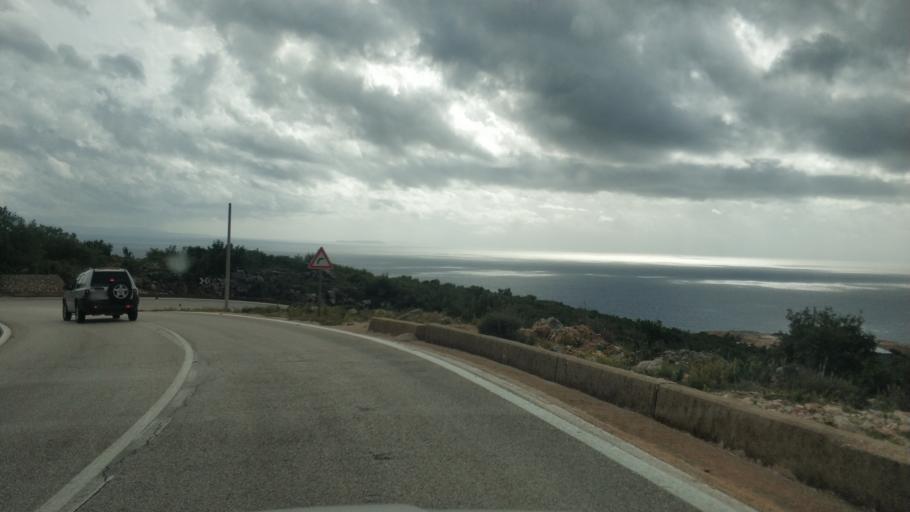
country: AL
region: Vlore
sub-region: Rrethi i Vlores
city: Vranisht
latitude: 40.1436
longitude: 19.6525
